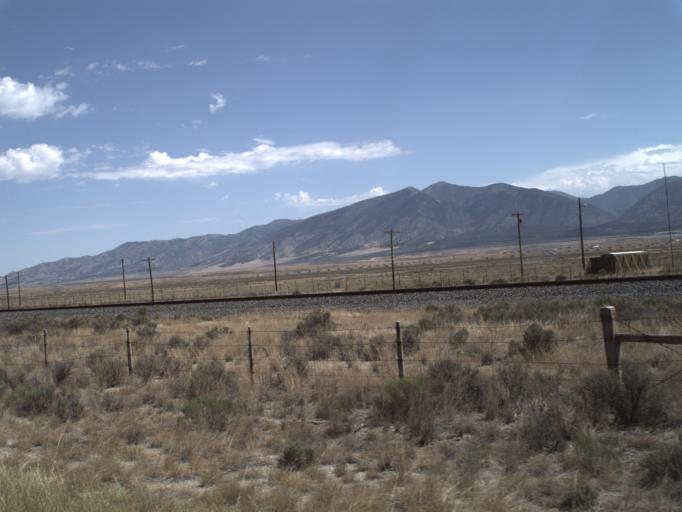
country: US
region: Utah
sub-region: Tooele County
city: Tooele
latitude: 40.2867
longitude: -112.3999
